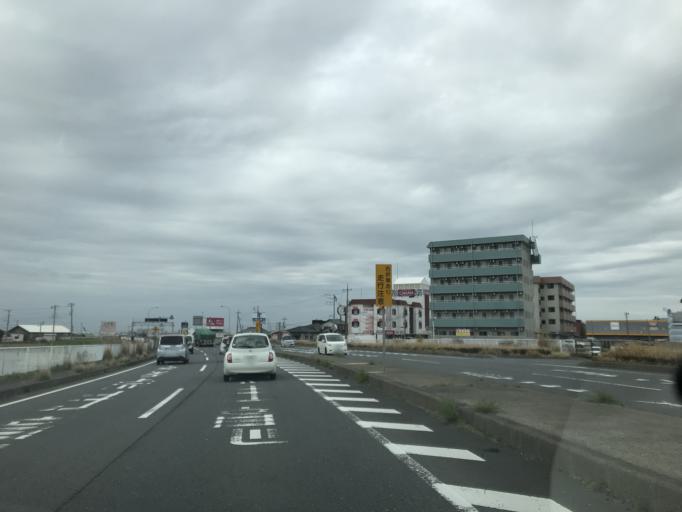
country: JP
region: Chiba
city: Katori-shi
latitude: 35.9153
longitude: 140.4890
